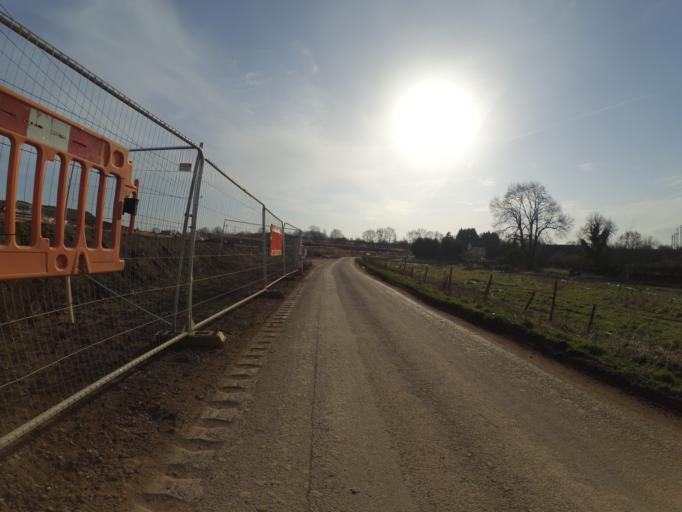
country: GB
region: England
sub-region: Warwickshire
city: Rugby
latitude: 52.3588
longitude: -1.1977
